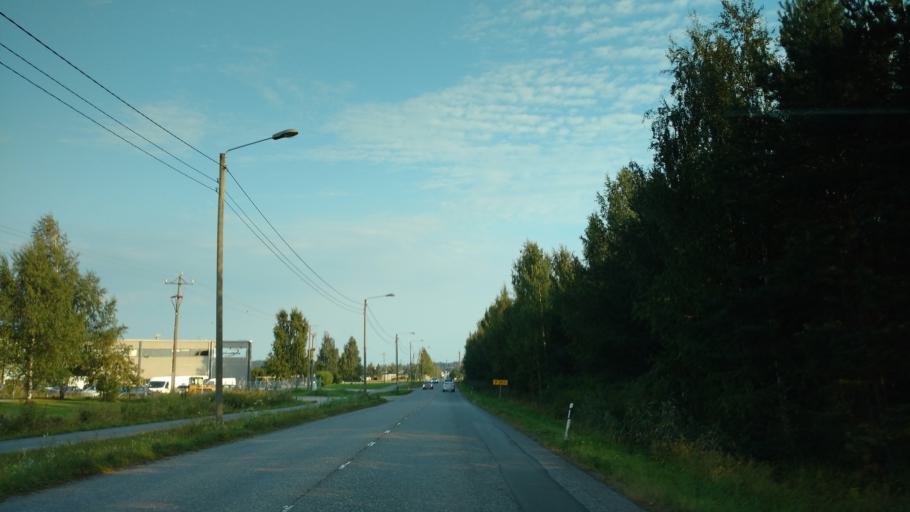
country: FI
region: Varsinais-Suomi
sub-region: Salo
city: Halikko
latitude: 60.3862
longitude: 23.0977
